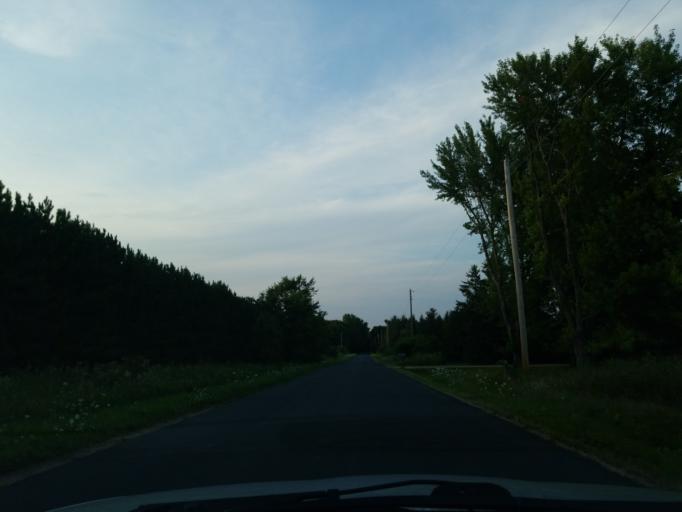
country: US
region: Minnesota
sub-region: Washington County
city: Stillwater
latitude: 45.0810
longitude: -92.7713
